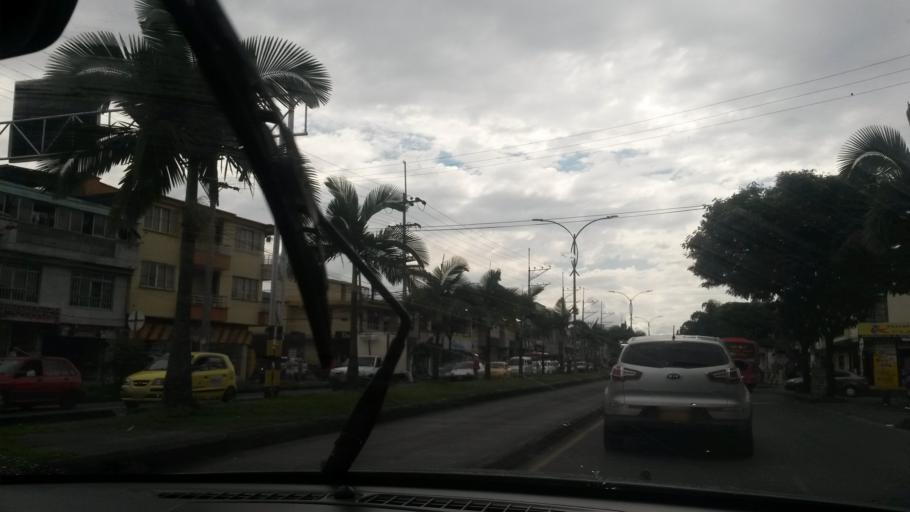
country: CO
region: Risaralda
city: Dos Quebradas
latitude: 4.8282
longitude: -75.6807
